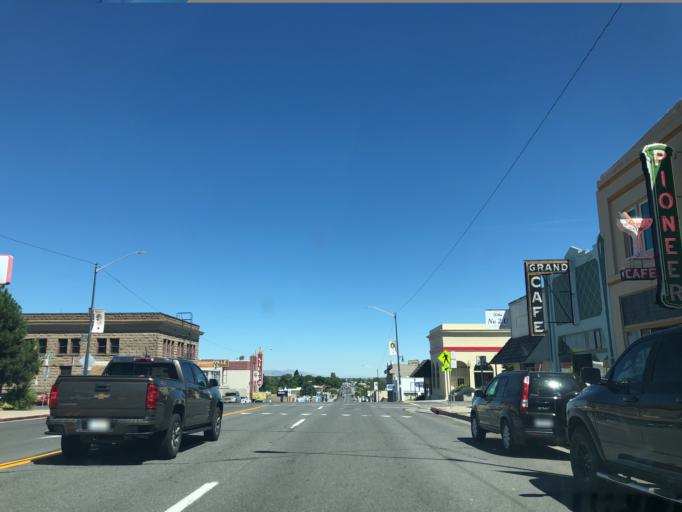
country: US
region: California
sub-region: Lassen County
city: Susanville
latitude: 40.4184
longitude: -120.6614
